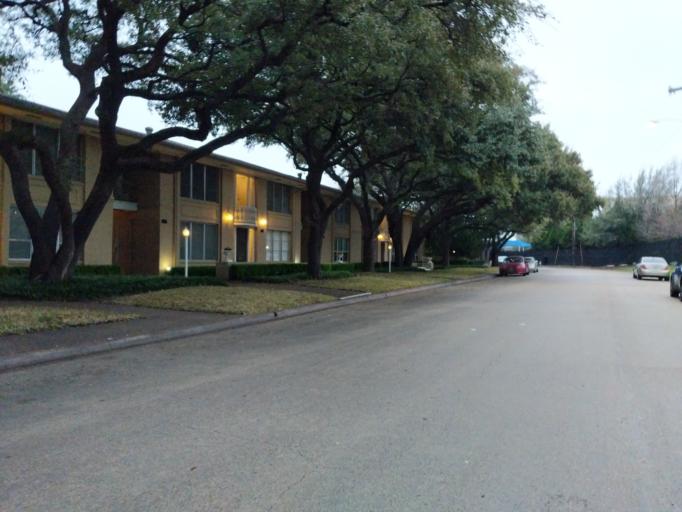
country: US
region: Texas
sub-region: Dallas County
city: University Park
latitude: 32.9012
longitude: -96.7717
